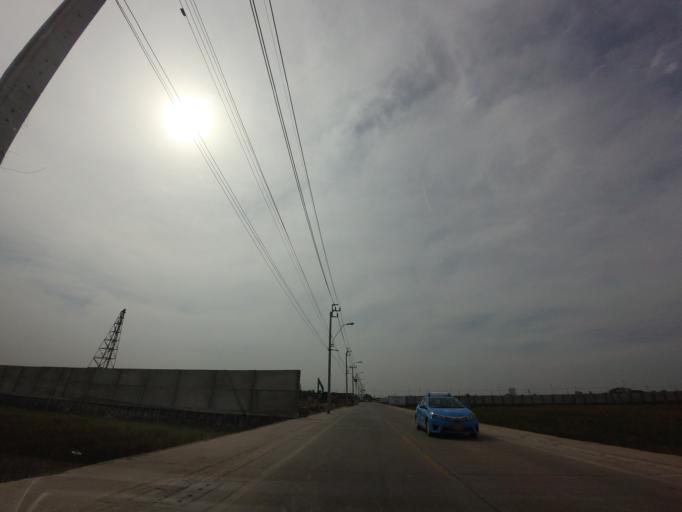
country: TH
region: Bangkok
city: Sai Mai
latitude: 13.8931
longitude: 100.6990
